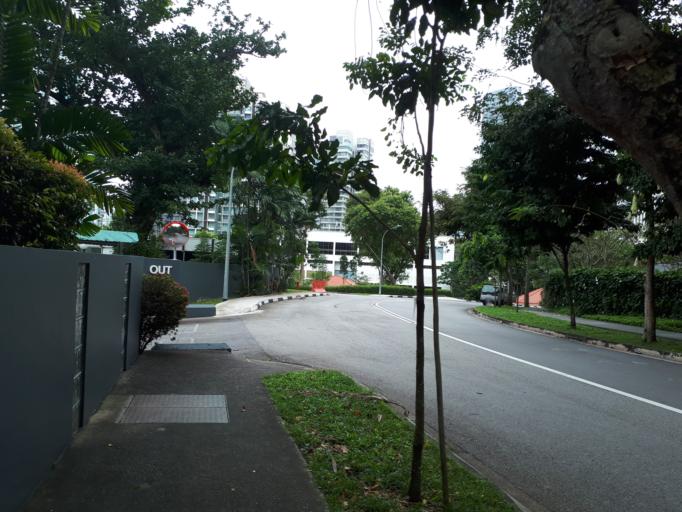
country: SG
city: Singapore
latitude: 1.2985
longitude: 103.8316
